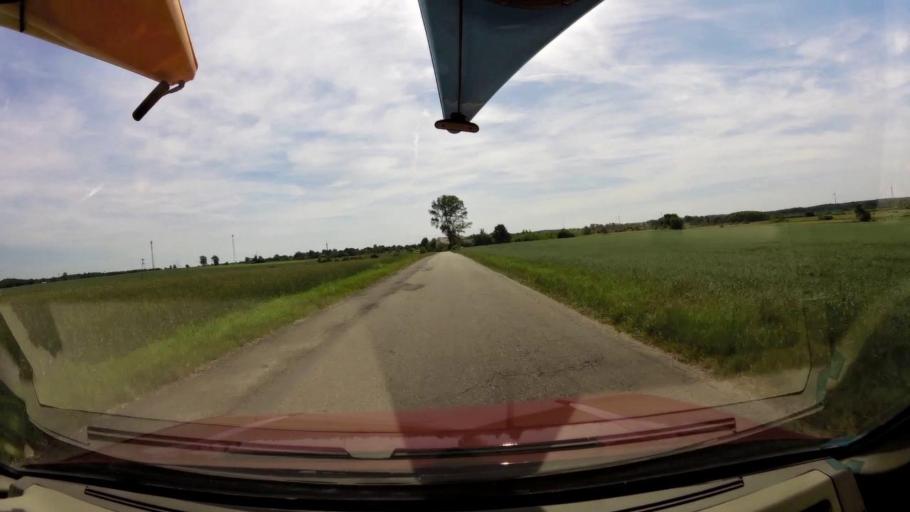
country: PL
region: West Pomeranian Voivodeship
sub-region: Powiat slawienski
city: Darlowo
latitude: 54.3236
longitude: 16.3963
